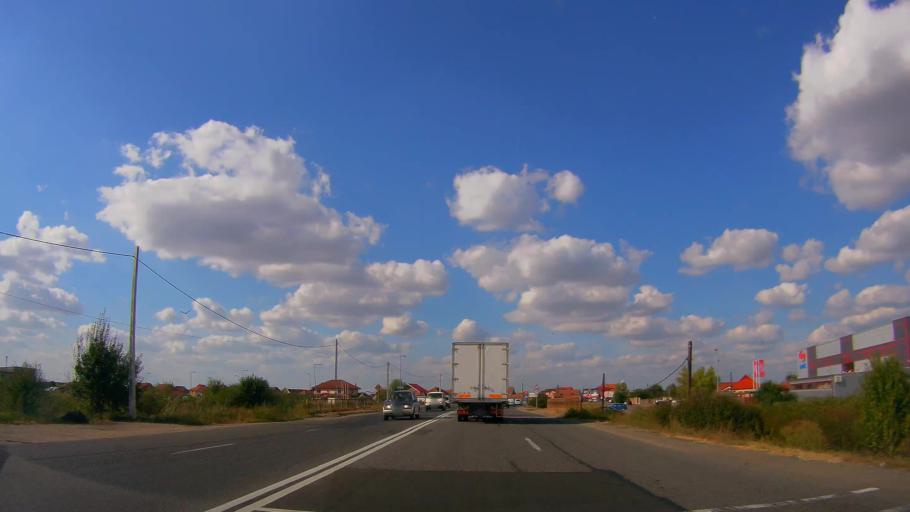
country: RO
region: Satu Mare
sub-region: Oras Ardud
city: Madaras
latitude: 47.7284
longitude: 22.8833
